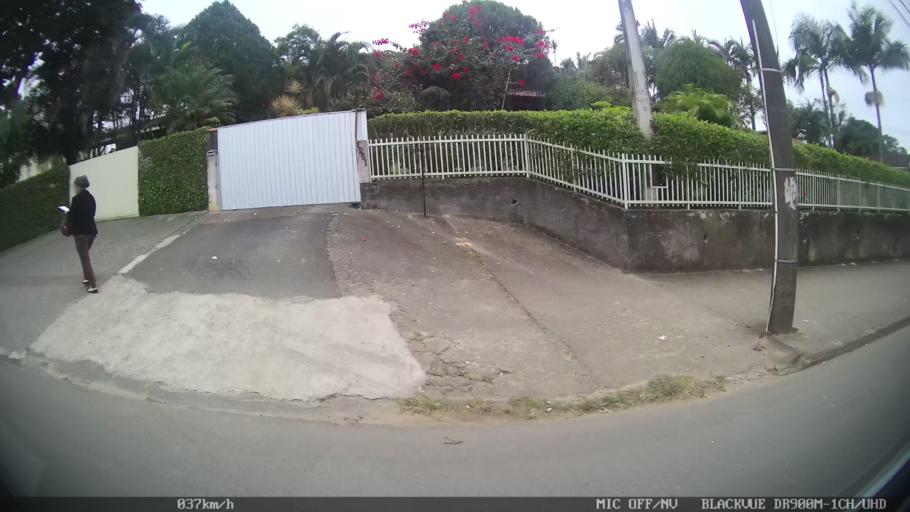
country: BR
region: Santa Catarina
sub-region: Joinville
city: Joinville
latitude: -26.3510
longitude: -48.8190
